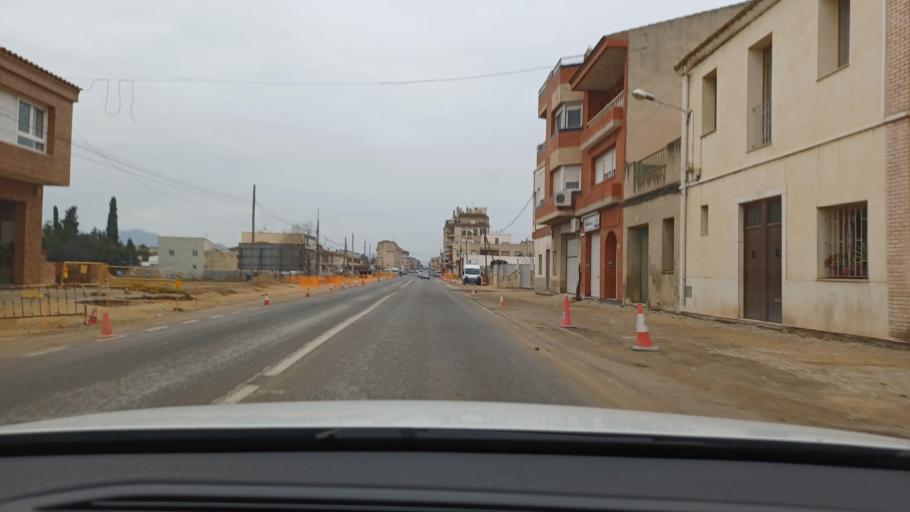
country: ES
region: Catalonia
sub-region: Provincia de Tarragona
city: Amposta
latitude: 40.7446
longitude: 0.6169
